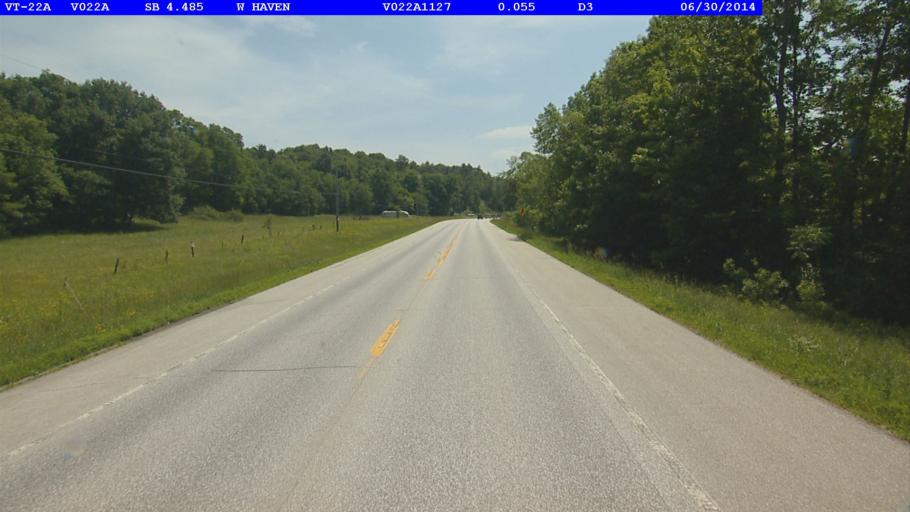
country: US
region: Vermont
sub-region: Rutland County
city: Fair Haven
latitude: 43.6293
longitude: -73.2969
